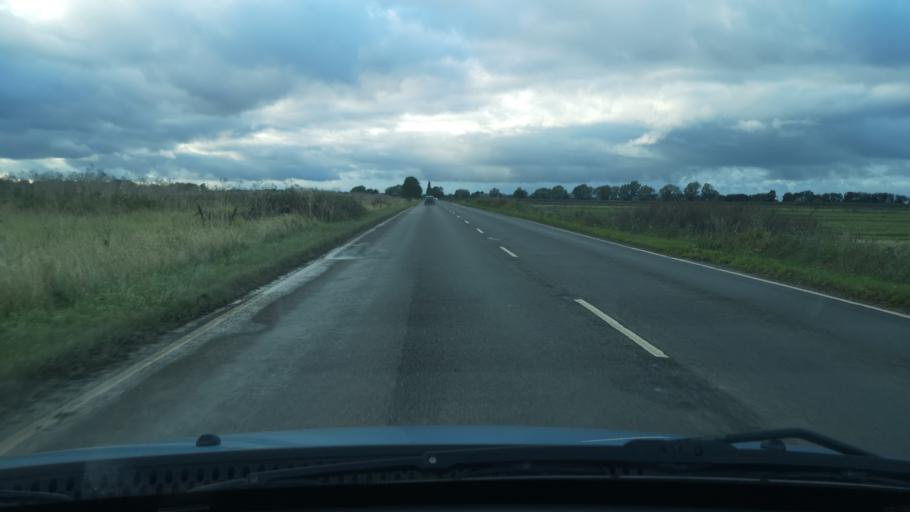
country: GB
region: England
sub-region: North Lincolnshire
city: Gunness
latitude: 53.5783
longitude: -0.7673
